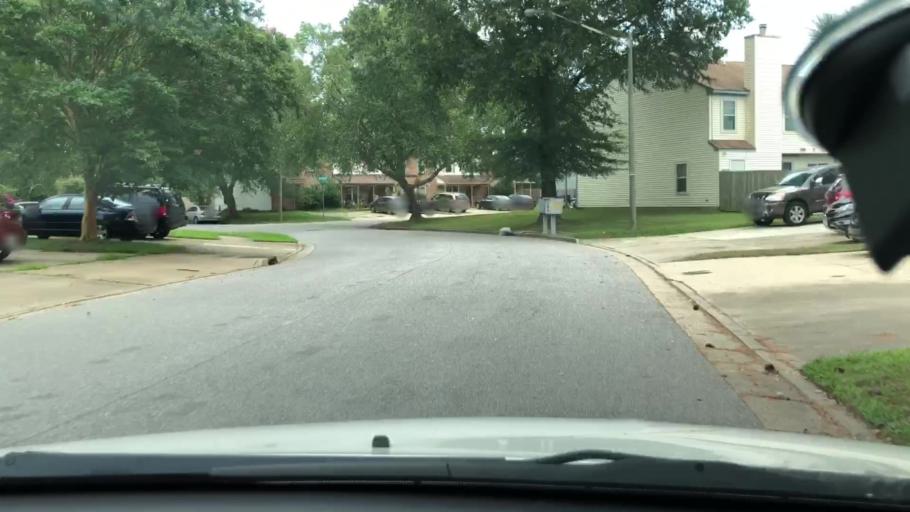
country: US
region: Virginia
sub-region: City of Virginia Beach
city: Virginia Beach
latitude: 36.8435
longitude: -76.1128
